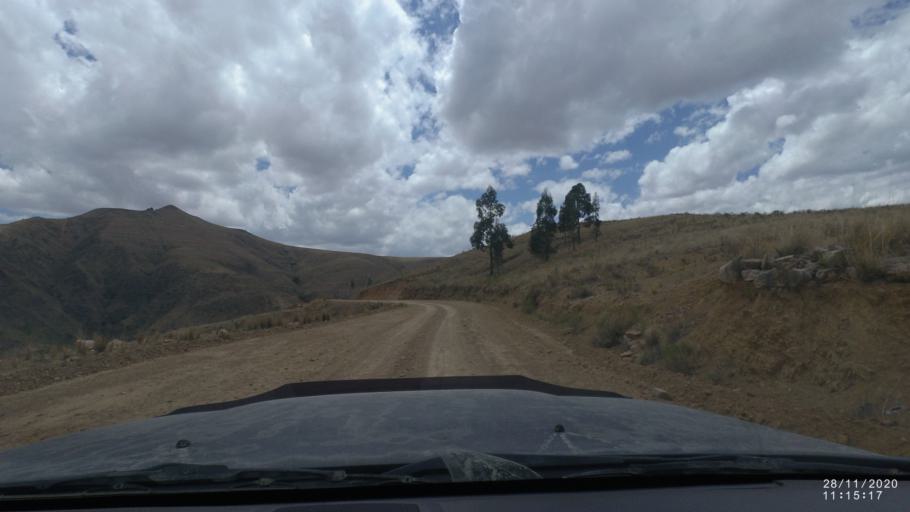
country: BO
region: Cochabamba
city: Tarata
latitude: -17.7447
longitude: -66.0905
